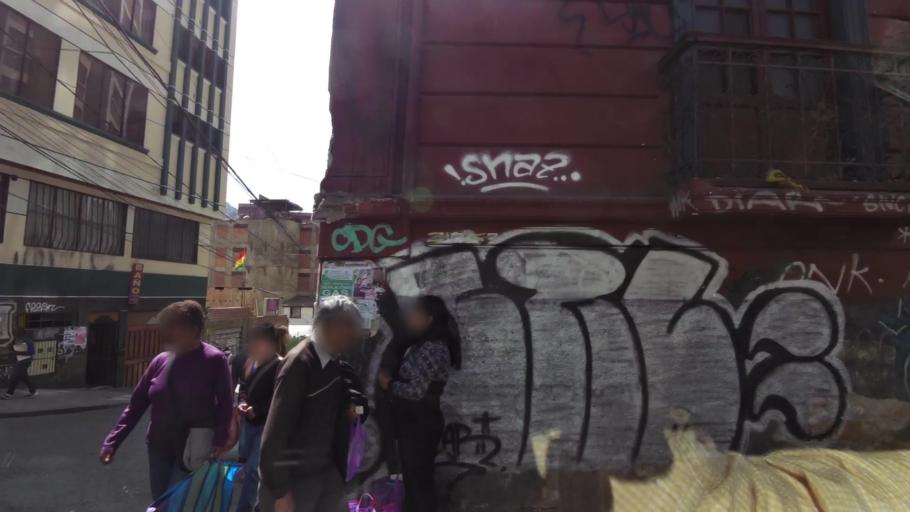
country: BO
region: La Paz
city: La Paz
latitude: -16.4997
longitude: -68.1361
